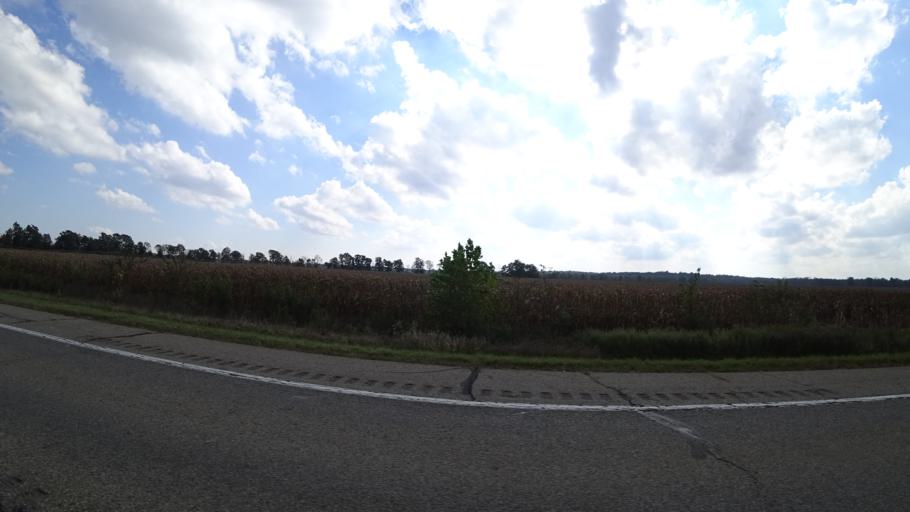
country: US
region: Michigan
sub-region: Branch County
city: Union City
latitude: 42.1059
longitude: -85.0197
